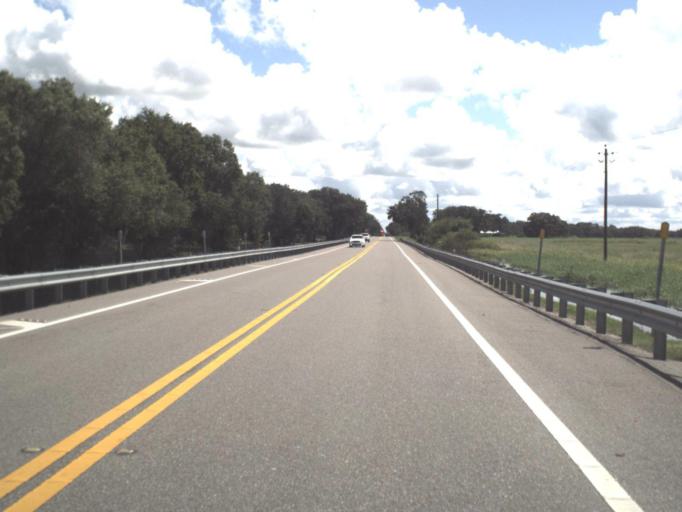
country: US
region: Florida
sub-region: Sarasota County
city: Lake Sarasota
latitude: 27.3853
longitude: -82.2455
